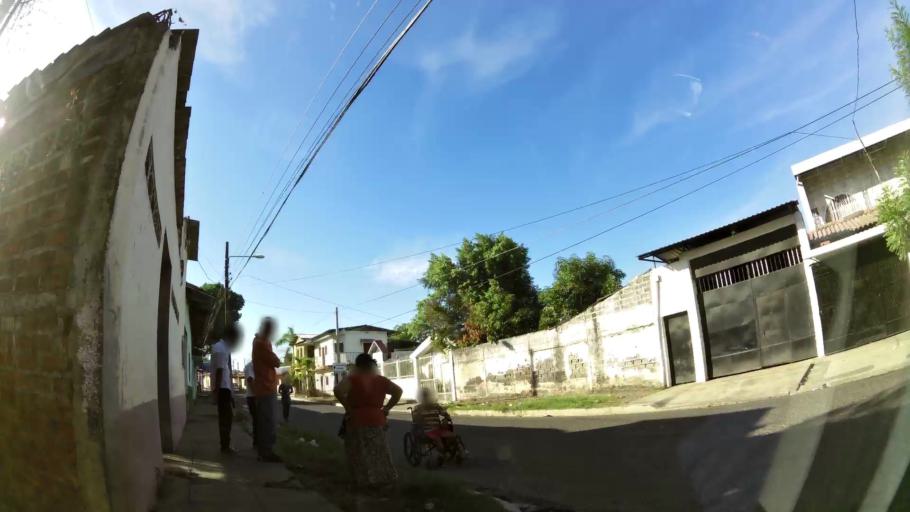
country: SV
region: San Miguel
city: San Miguel
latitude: 13.4683
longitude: -88.1859
